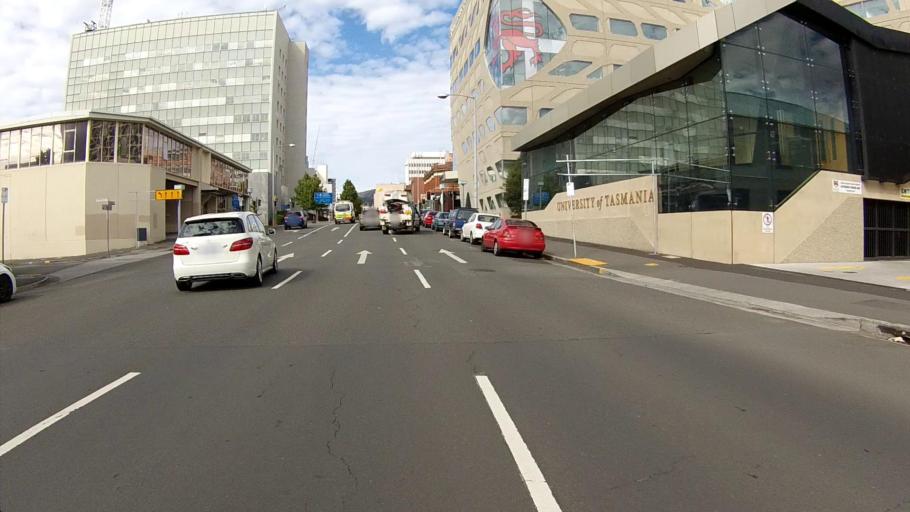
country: AU
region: Tasmania
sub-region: Hobart
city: Hobart
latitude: -42.8785
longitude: 147.3305
